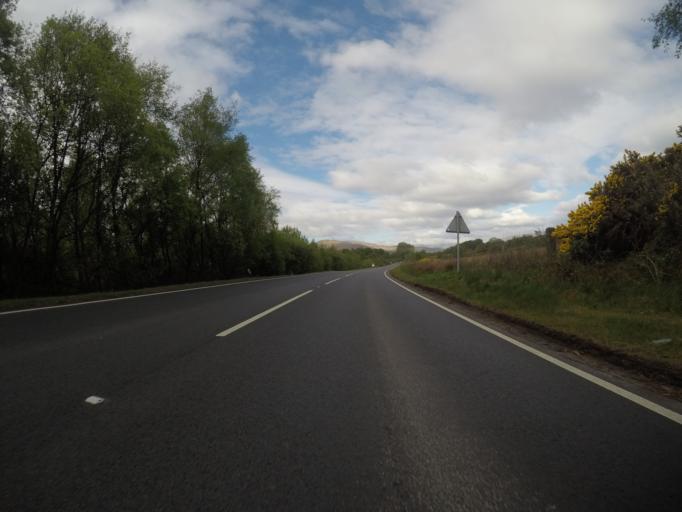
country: GB
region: Scotland
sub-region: Highland
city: Fort William
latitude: 56.8392
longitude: -5.0597
